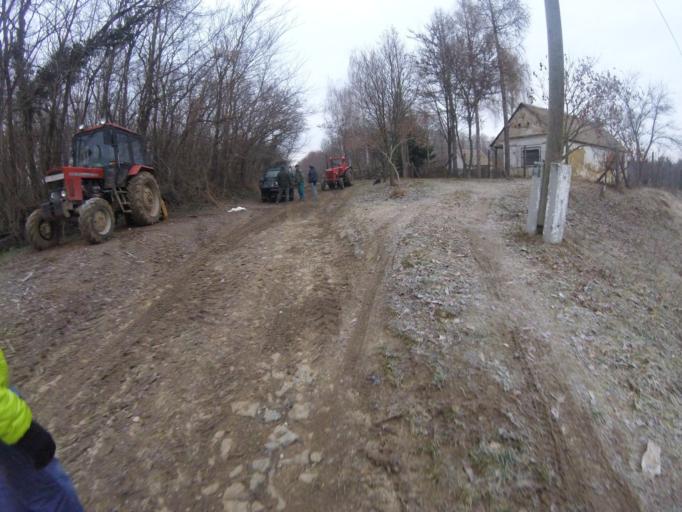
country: HU
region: Baranya
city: Pecsvarad
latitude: 46.1290
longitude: 18.5270
